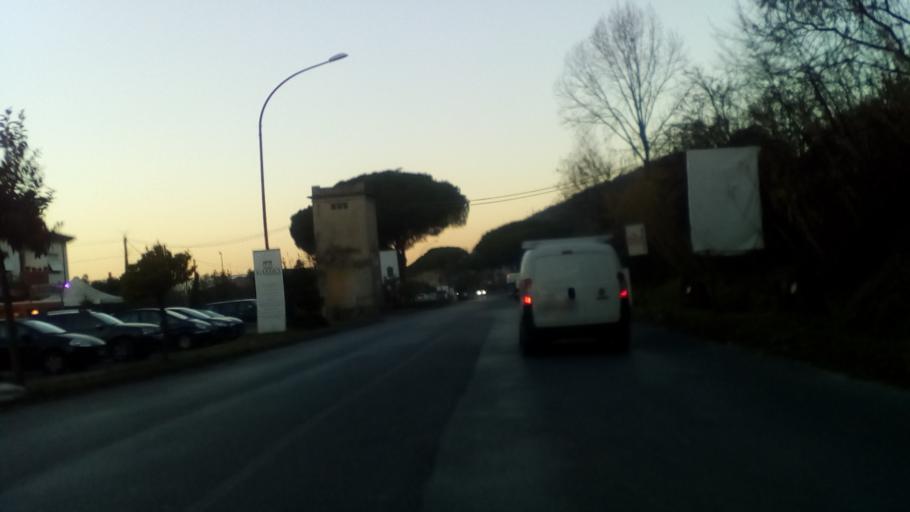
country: IT
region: Tuscany
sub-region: Provincia di Massa-Carrara
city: Massa
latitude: 44.0379
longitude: 10.0972
